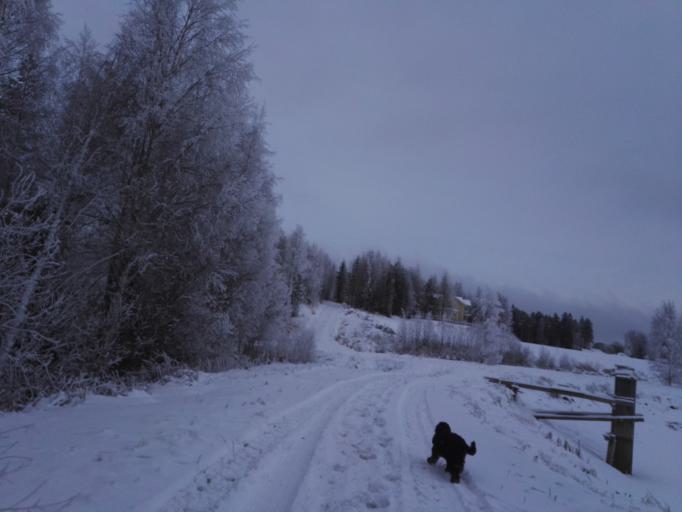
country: FI
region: Satakunta
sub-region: Pohjois-Satakunta
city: Jaemijaervi
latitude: 61.7835
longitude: 22.8772
